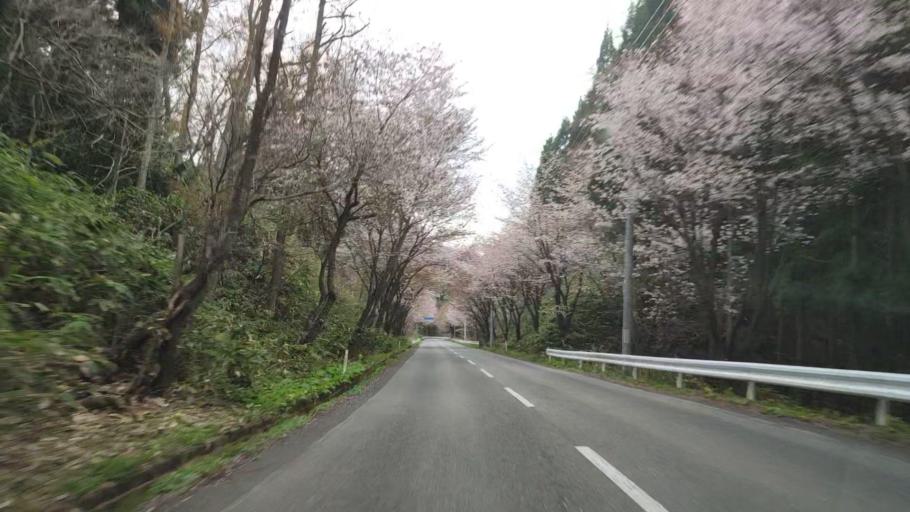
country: JP
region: Akita
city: Hanawa
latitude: 40.3659
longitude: 140.7853
